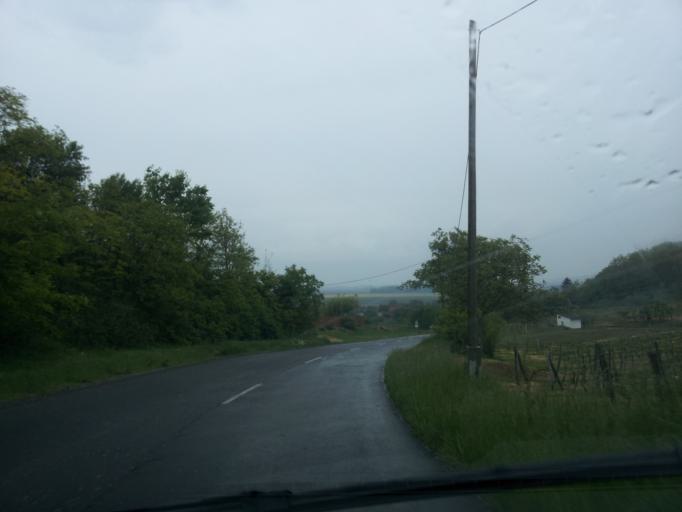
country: HU
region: Tolna
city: Szekszard
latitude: 46.2971
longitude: 18.6830
